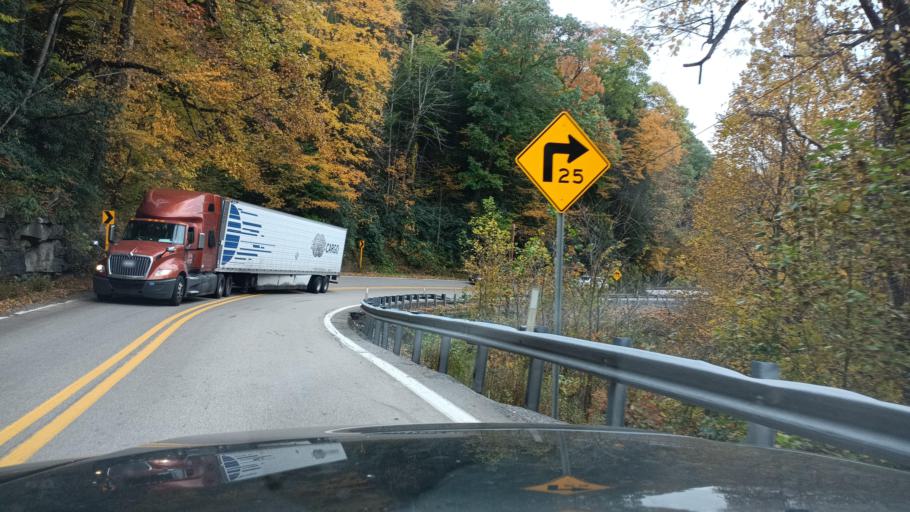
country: US
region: West Virginia
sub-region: Preston County
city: Terra Alta
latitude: 39.2970
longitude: -79.6174
